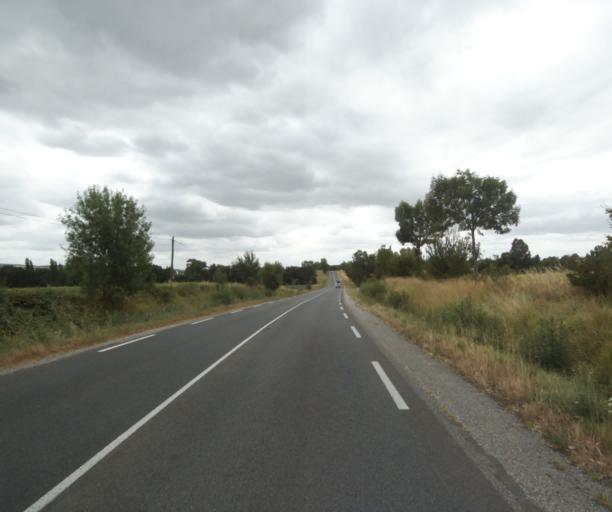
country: FR
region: Midi-Pyrenees
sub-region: Departement de la Haute-Garonne
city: Revel
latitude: 43.4876
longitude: 2.0336
